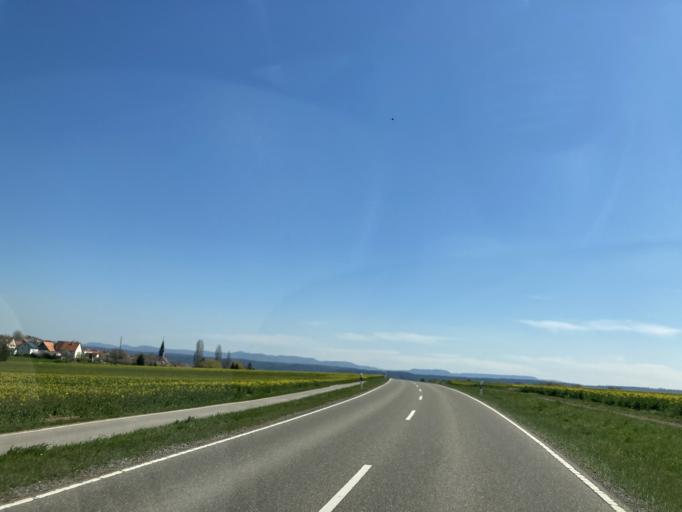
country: DE
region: Baden-Wuerttemberg
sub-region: Tuebingen Region
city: Rottenburg
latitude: 48.5097
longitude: 8.9275
